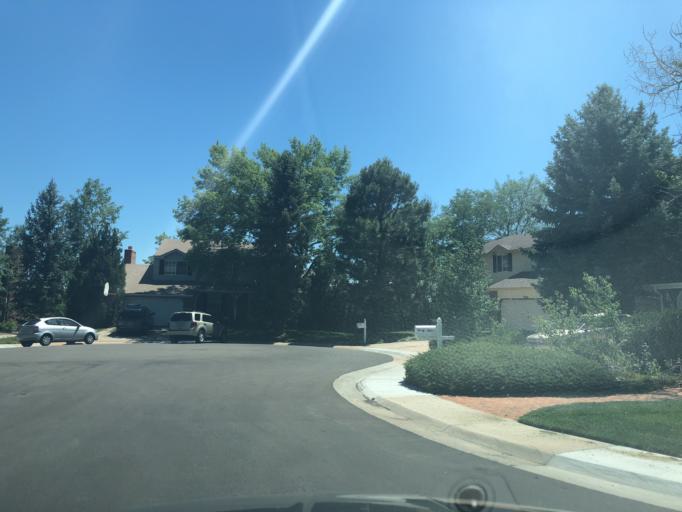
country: US
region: Colorado
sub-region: Arapahoe County
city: Dove Valley
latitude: 39.6172
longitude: -104.7890
